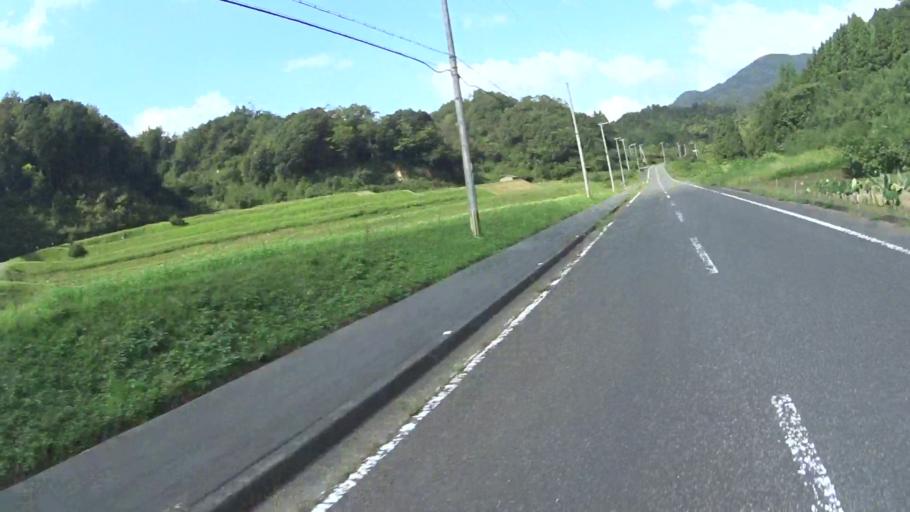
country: JP
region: Kyoto
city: Miyazu
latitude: 35.6270
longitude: 135.2369
